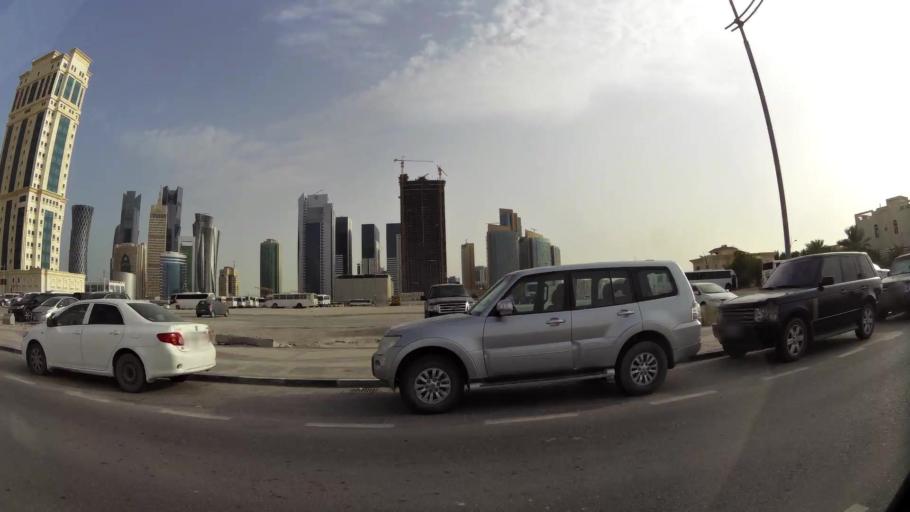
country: QA
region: Baladiyat ad Dawhah
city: Doha
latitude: 25.3256
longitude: 51.5209
